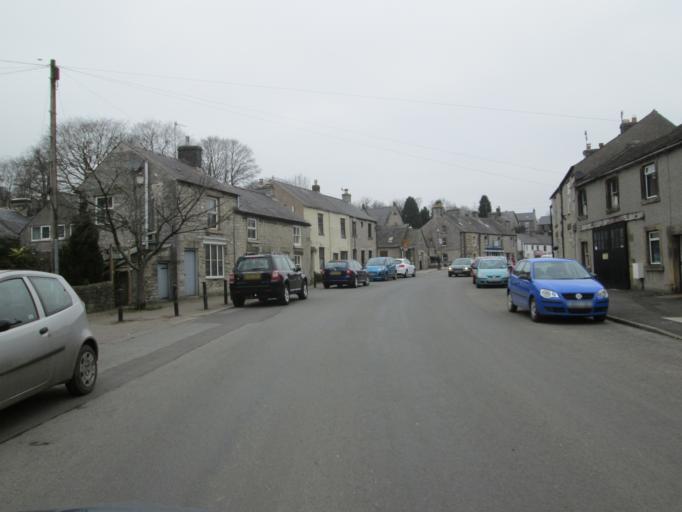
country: GB
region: England
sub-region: Derbyshire
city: Tideswell
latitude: 53.2763
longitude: -1.7744
